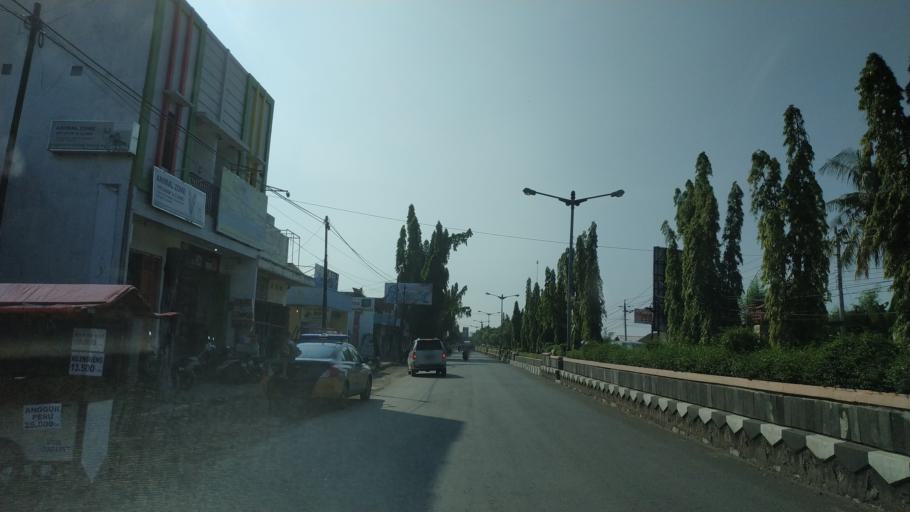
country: ID
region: Central Java
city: Pemalang
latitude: -6.8913
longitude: 109.3968
